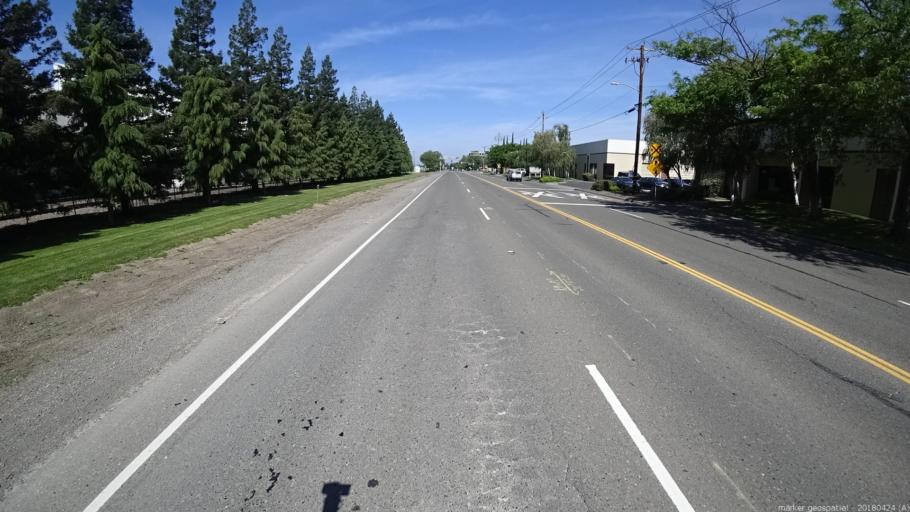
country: US
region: California
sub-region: Yolo County
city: West Sacramento
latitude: 38.5678
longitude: -121.5471
